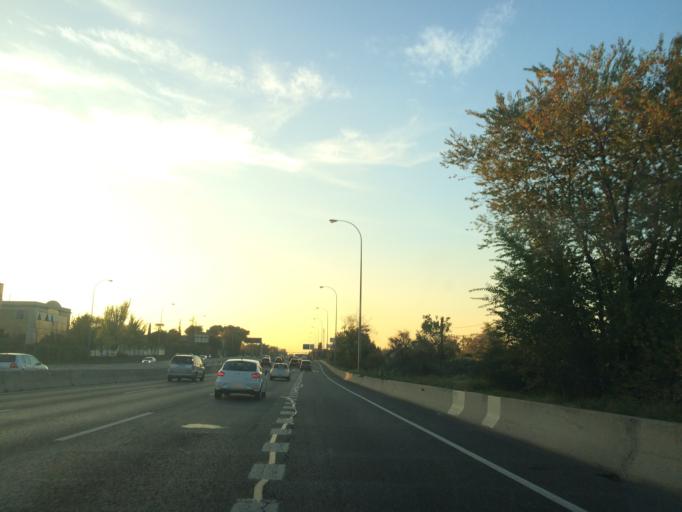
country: ES
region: Madrid
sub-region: Provincia de Madrid
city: Moncloa-Aravaca
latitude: 40.4624
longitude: -3.7718
